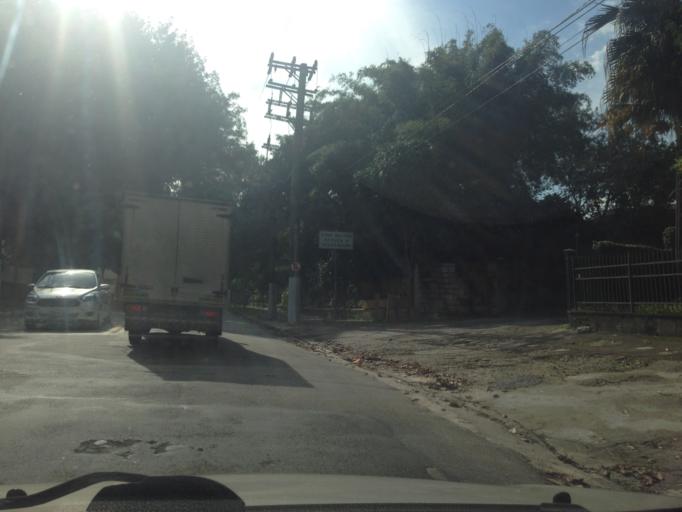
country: BR
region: Sao Paulo
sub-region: Sao Paulo
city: Sao Paulo
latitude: -23.5203
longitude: -46.7115
